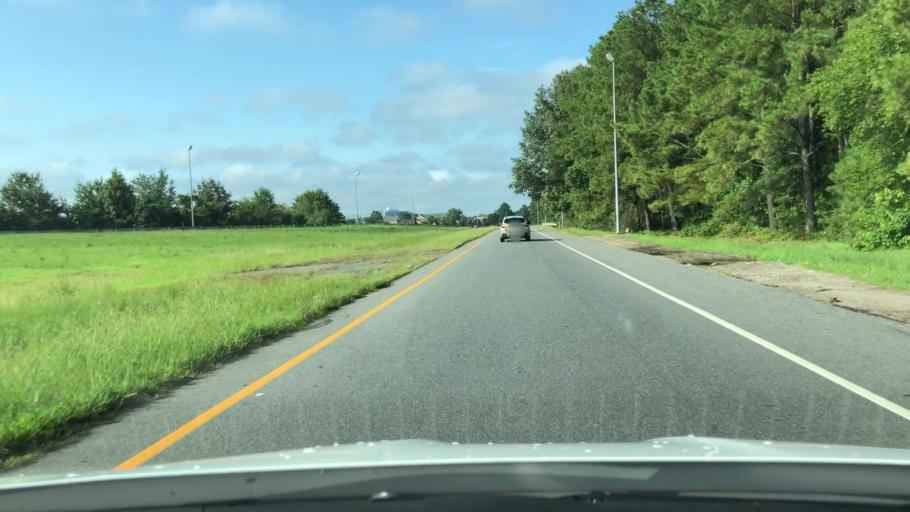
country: US
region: Virginia
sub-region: City of Chesapeake
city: Chesapeake
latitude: 36.7866
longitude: -76.2356
